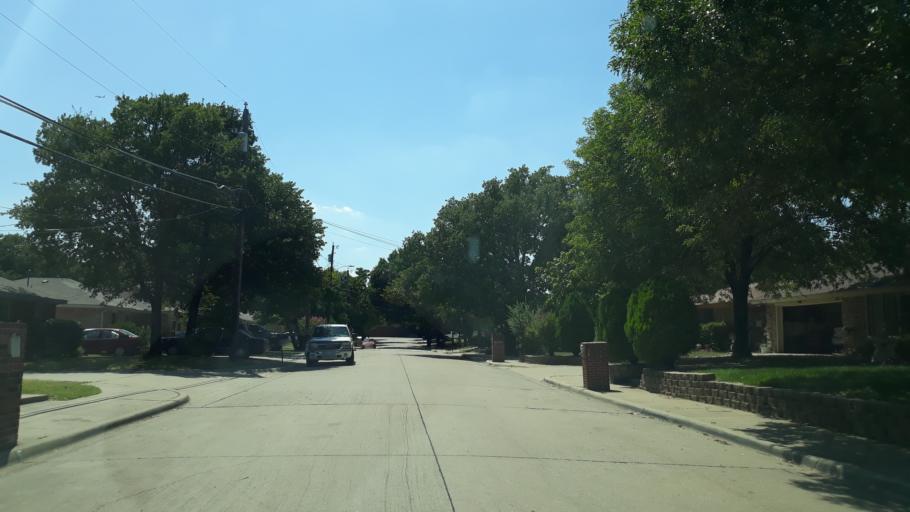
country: US
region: Texas
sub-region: Dallas County
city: Irving
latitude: 32.8252
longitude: -97.0025
